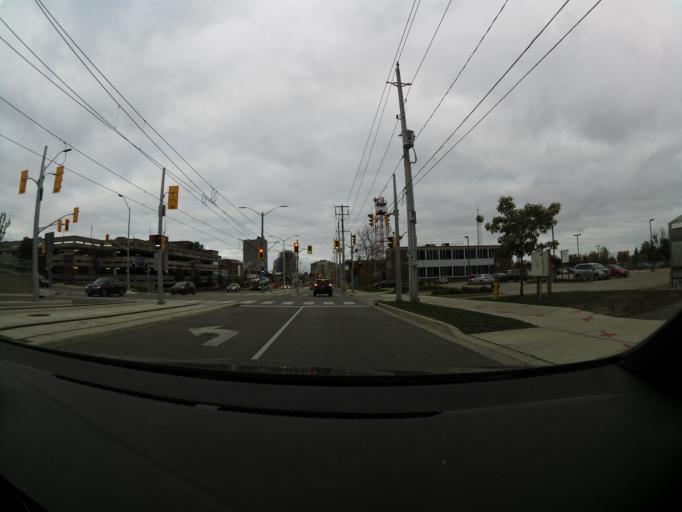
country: CA
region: Ontario
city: Waterloo
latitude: 43.4564
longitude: -80.5093
